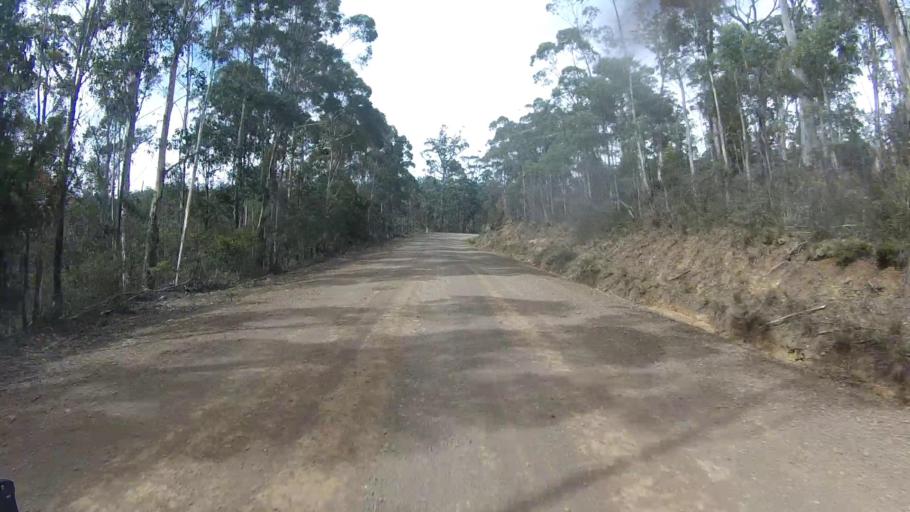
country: AU
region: Tasmania
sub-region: Sorell
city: Sorell
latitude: -42.6833
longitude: 147.8804
